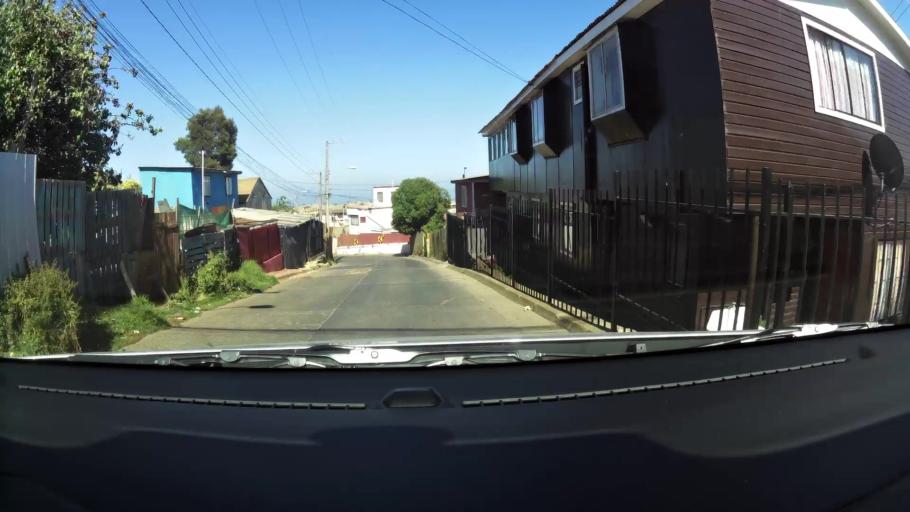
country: CL
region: Valparaiso
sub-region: Provincia de Valparaiso
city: Valparaiso
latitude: -33.0540
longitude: -71.6494
